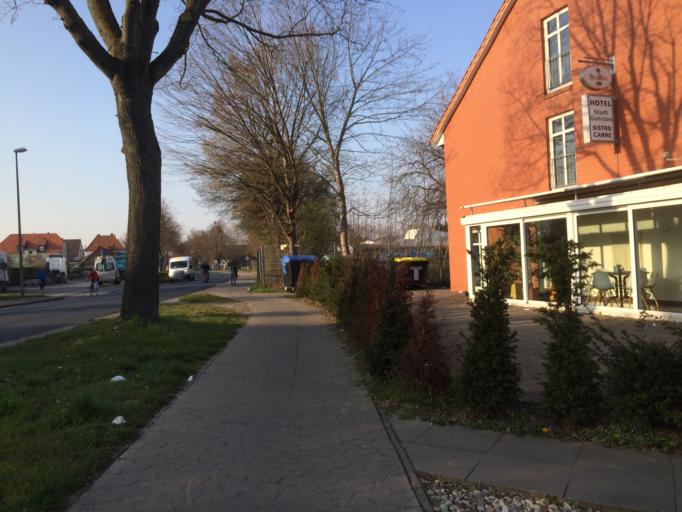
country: DE
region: Lower Saxony
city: Gehrden
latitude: 52.3096
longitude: 9.6076
